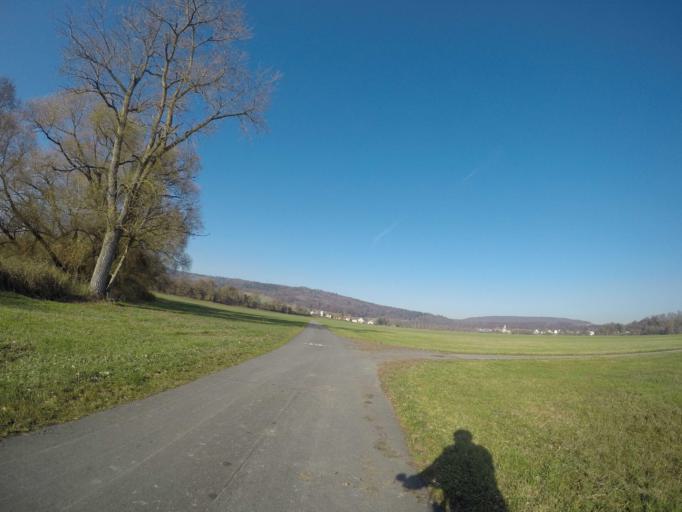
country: DE
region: Baden-Wuerttemberg
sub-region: Tuebingen Region
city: Unlingen
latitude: 48.1920
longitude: 9.5026
